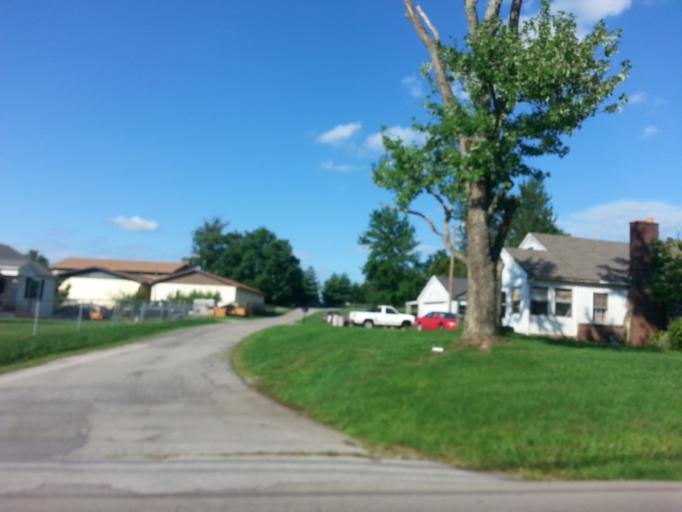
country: US
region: Tennessee
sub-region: Blount County
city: Maryville
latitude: 35.7133
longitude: -84.0146
